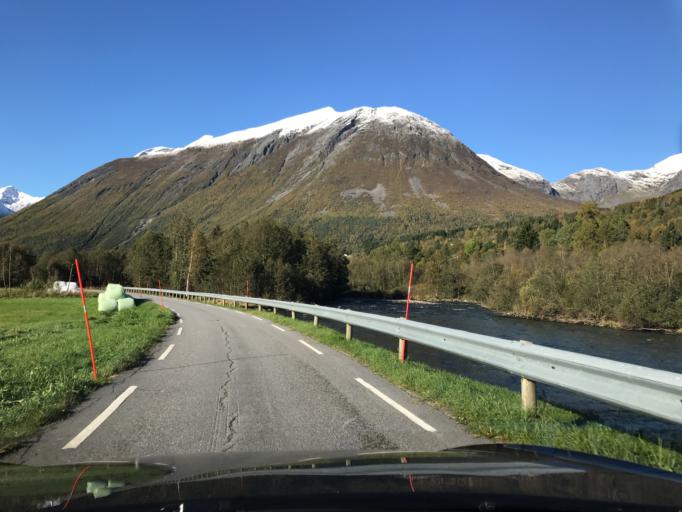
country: NO
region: More og Romsdal
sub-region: Norddal
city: Valldal
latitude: 62.3311
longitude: 7.3741
